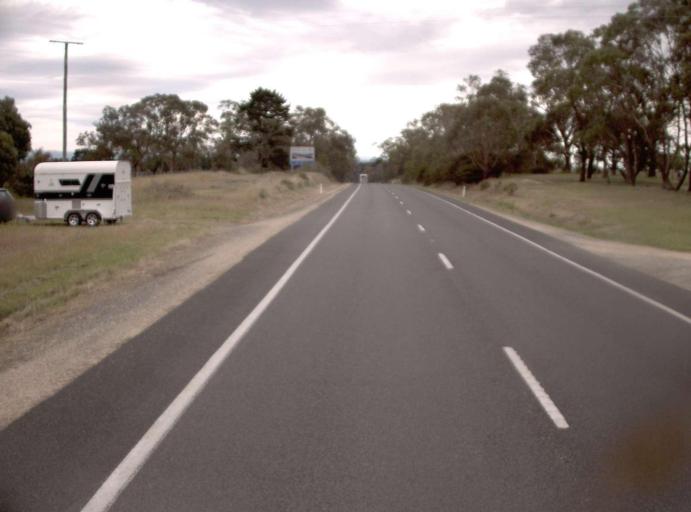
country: AU
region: Victoria
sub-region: Wellington
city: Sale
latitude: -38.1813
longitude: 147.0834
